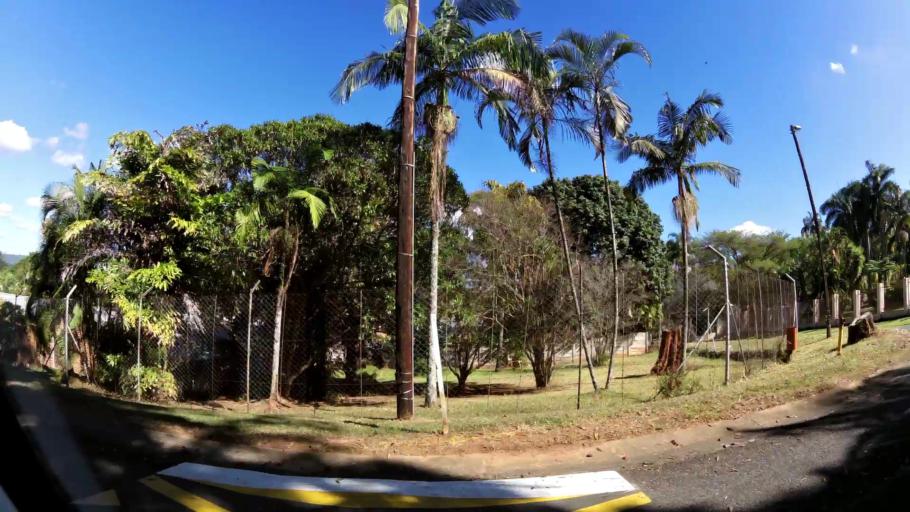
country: ZA
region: Limpopo
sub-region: Mopani District Municipality
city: Tzaneen
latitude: -23.8246
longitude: 30.1470
